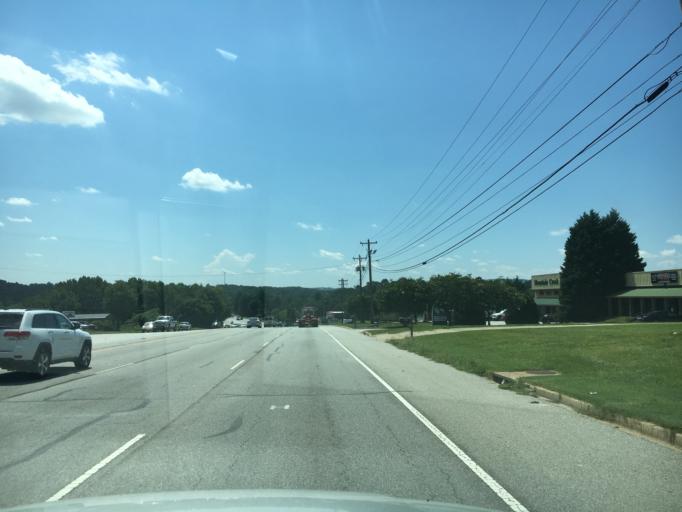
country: US
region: South Carolina
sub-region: Greenville County
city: Taylors
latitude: 34.9290
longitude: -82.2965
